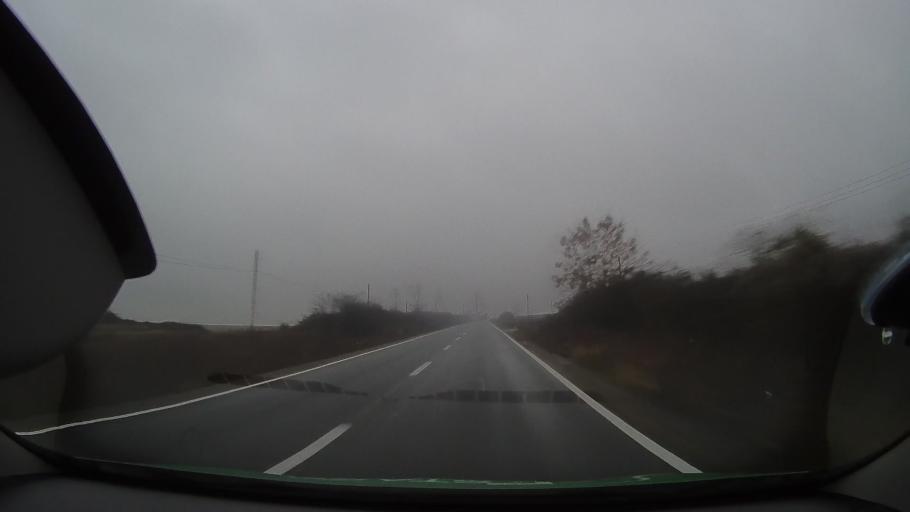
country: RO
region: Bihor
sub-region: Comuna Olcea
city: Calacea
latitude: 46.7184
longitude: 21.9522
